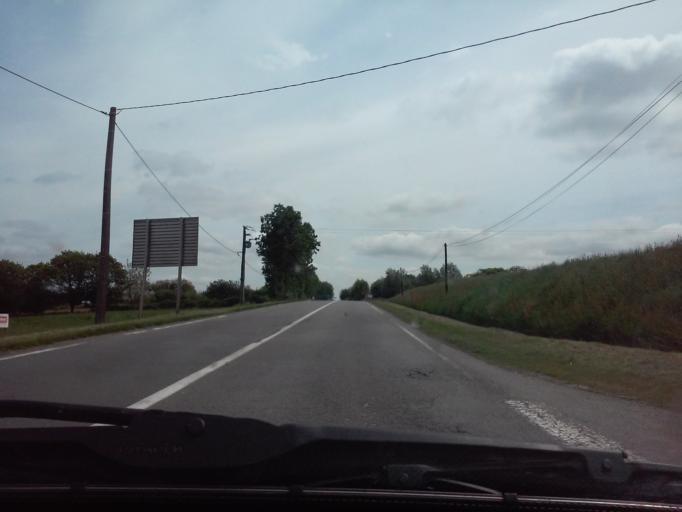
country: FR
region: Brittany
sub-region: Departement d'Ille-et-Vilaine
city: Fougeres
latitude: 48.3361
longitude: -1.1890
